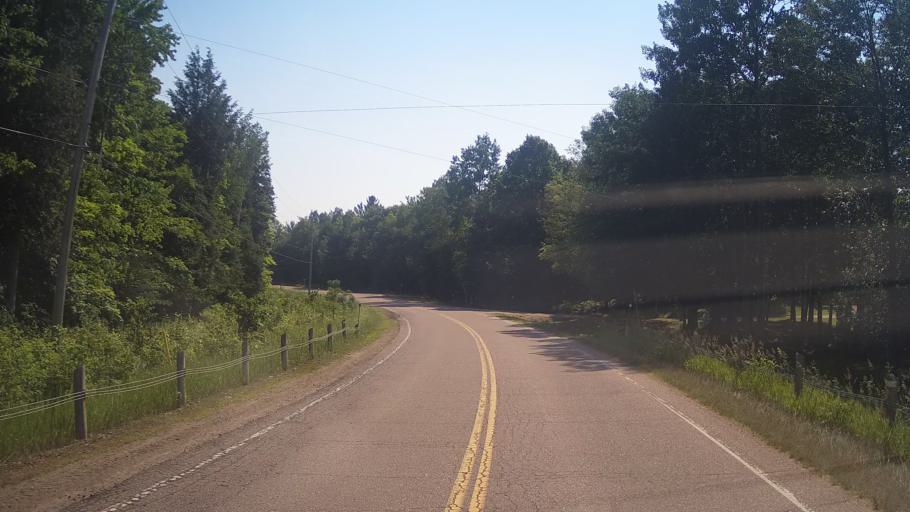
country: CA
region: Ontario
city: Pembroke
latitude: 45.6027
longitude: -77.2315
